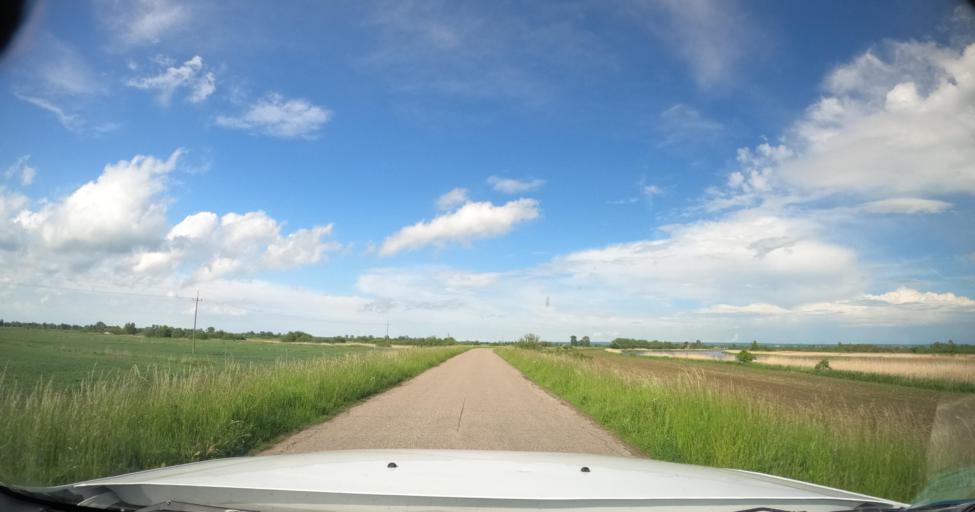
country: PL
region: Warmian-Masurian Voivodeship
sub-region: Powiat elblaski
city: Gronowo Elblaskie
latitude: 54.1856
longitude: 19.2803
